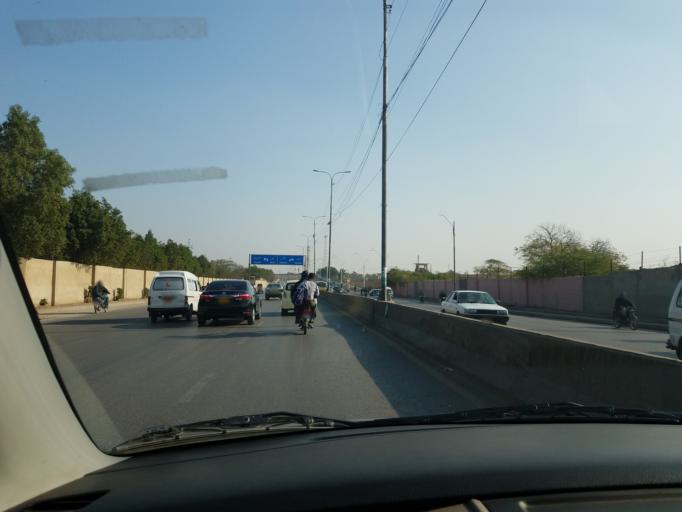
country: PK
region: Sindh
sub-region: Karachi District
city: Karachi
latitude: 24.8905
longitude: 67.1230
